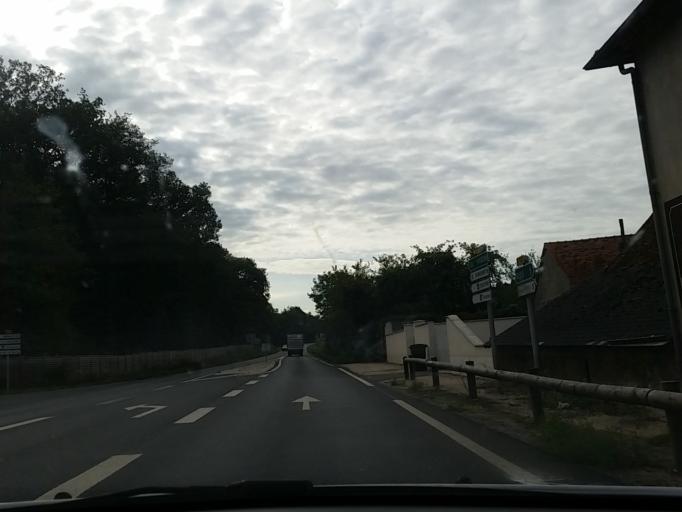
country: FR
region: Centre
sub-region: Departement du Loir-et-Cher
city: Cour-Cheverny
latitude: 47.5315
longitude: 1.4227
